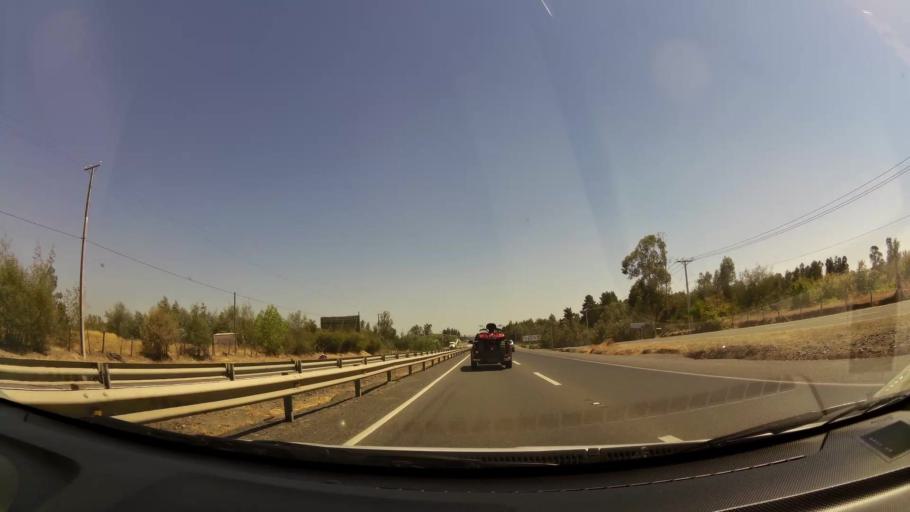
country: CL
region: Maule
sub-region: Provincia de Talca
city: Talca
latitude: -35.3340
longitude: -71.5566
